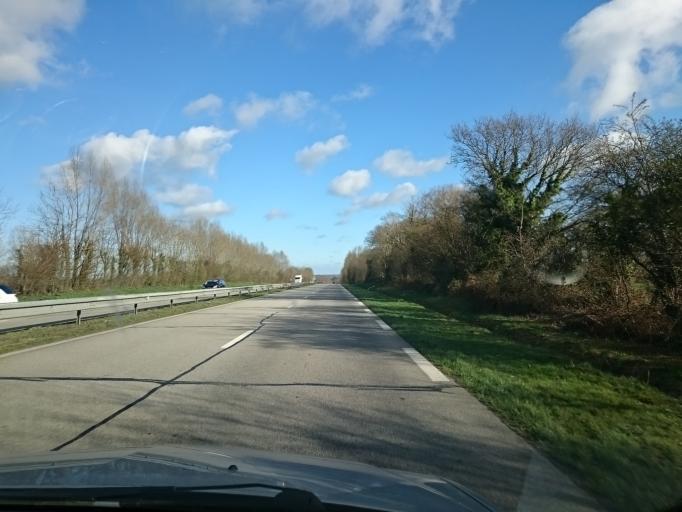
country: FR
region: Lower Normandy
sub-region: Departement de la Manche
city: Montebourg
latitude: 49.4881
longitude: -1.4004
